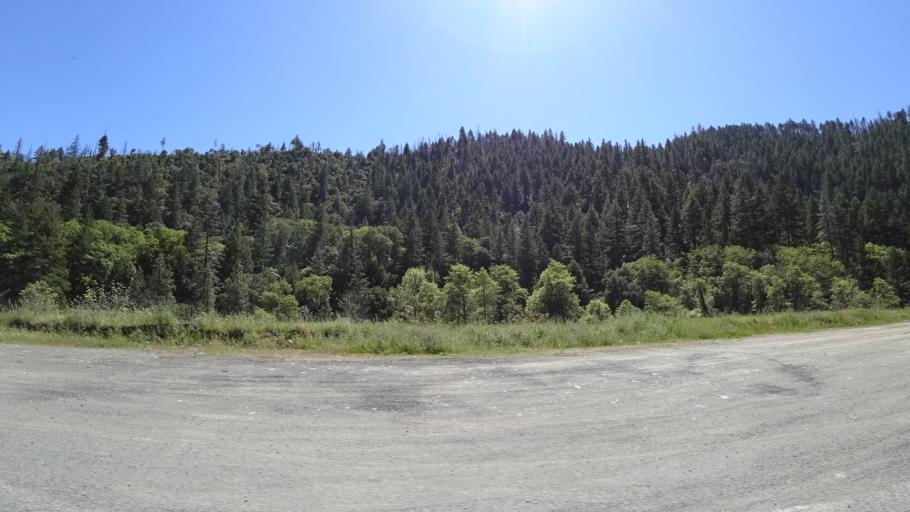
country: US
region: California
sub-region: Trinity County
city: Hayfork
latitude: 40.7619
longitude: -123.2874
